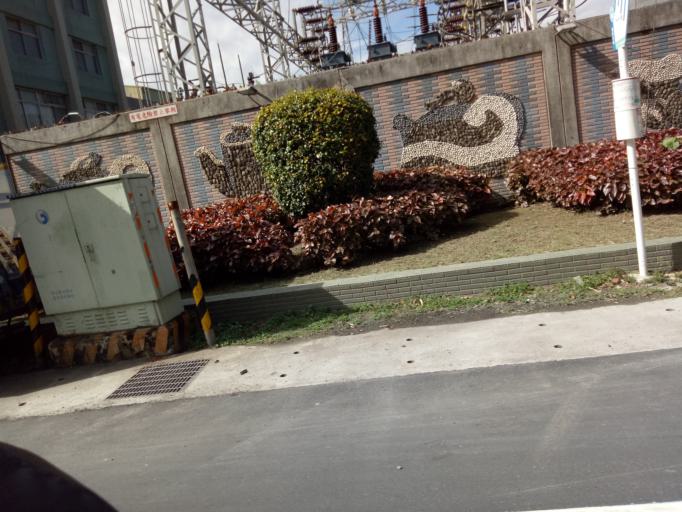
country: TW
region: Taiwan
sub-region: Taoyuan
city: Taoyuan
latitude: 24.9427
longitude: 121.3392
